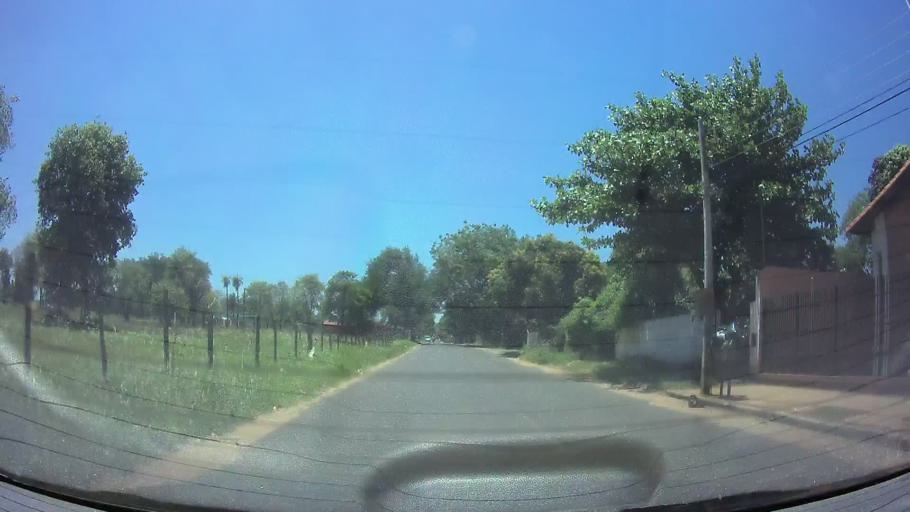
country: PY
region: Central
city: Fernando de la Mora
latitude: -25.2726
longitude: -57.5121
